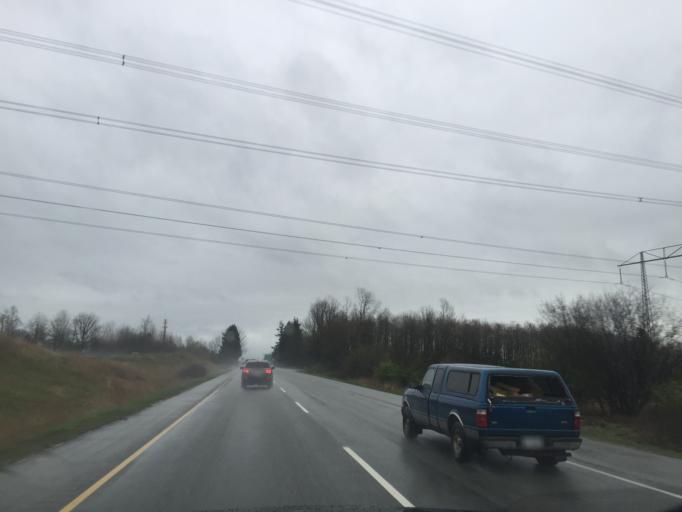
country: CA
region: British Columbia
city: Aldergrove
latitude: 49.0702
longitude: -122.4136
